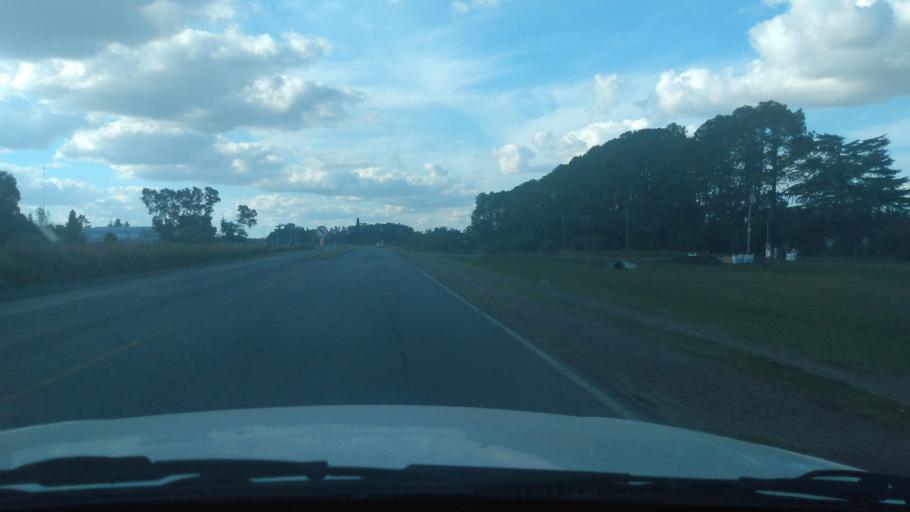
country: AR
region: Buenos Aires
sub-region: Partido de Mercedes
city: Mercedes
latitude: -34.6734
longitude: -59.4002
